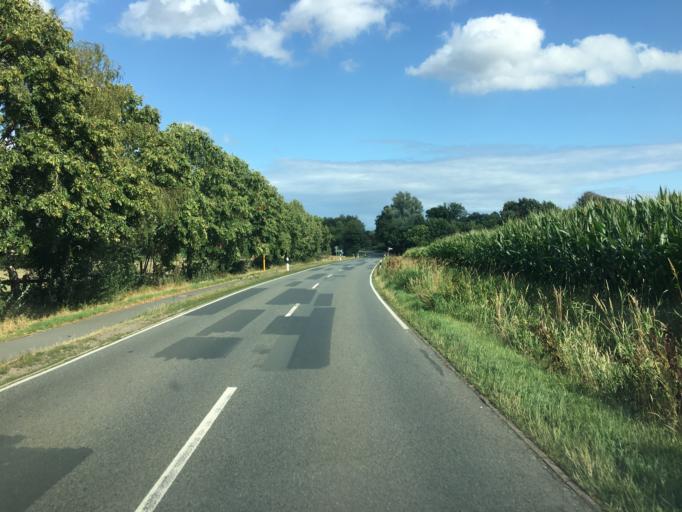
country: DE
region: Lower Saxony
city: Wardenburg
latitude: 53.0679
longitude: 8.1753
